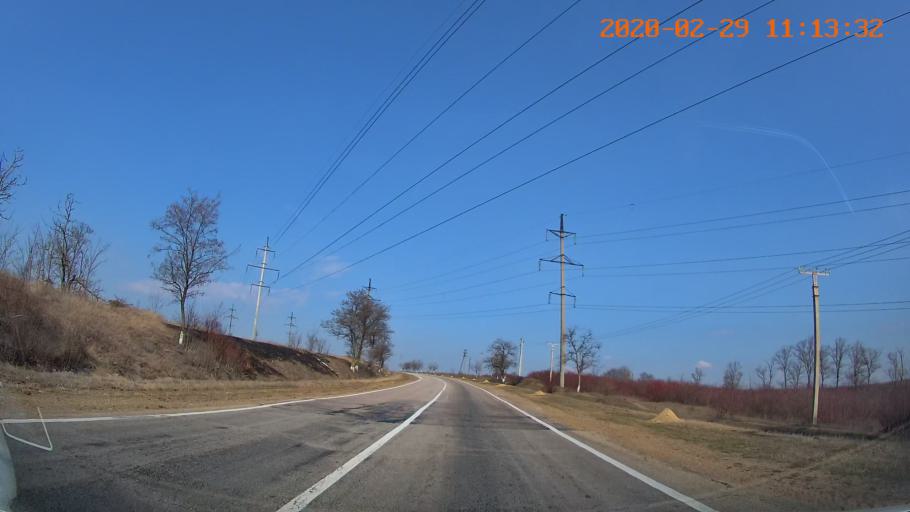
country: MD
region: Telenesti
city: Dubasari
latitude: 47.2730
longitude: 29.1809
